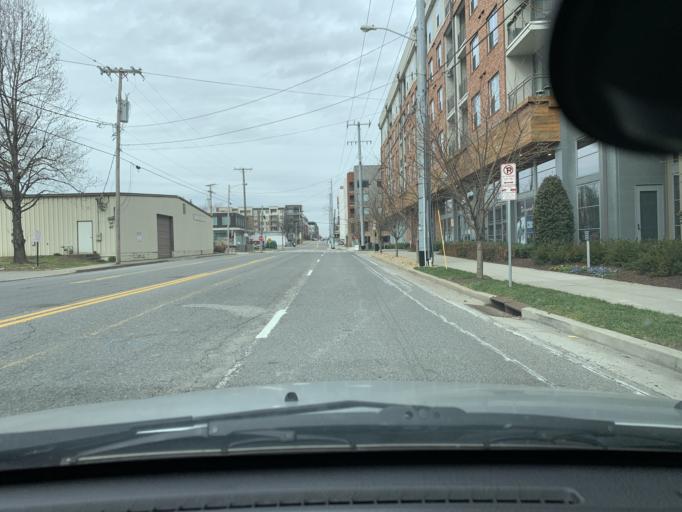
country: US
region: Tennessee
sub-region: Davidson County
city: Nashville
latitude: 36.1755
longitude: -86.7849
